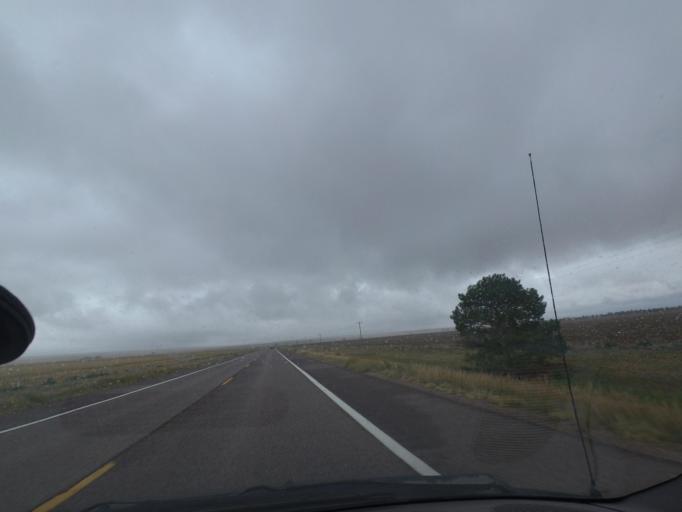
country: US
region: Colorado
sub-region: Arapahoe County
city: Byers
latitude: 39.7403
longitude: -104.0004
